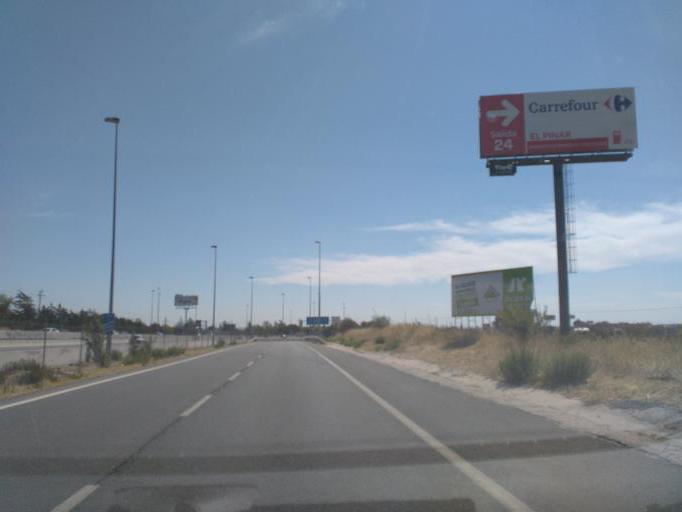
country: ES
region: Madrid
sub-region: Provincia de Madrid
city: Las Matas
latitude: 40.5630
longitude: -3.9059
